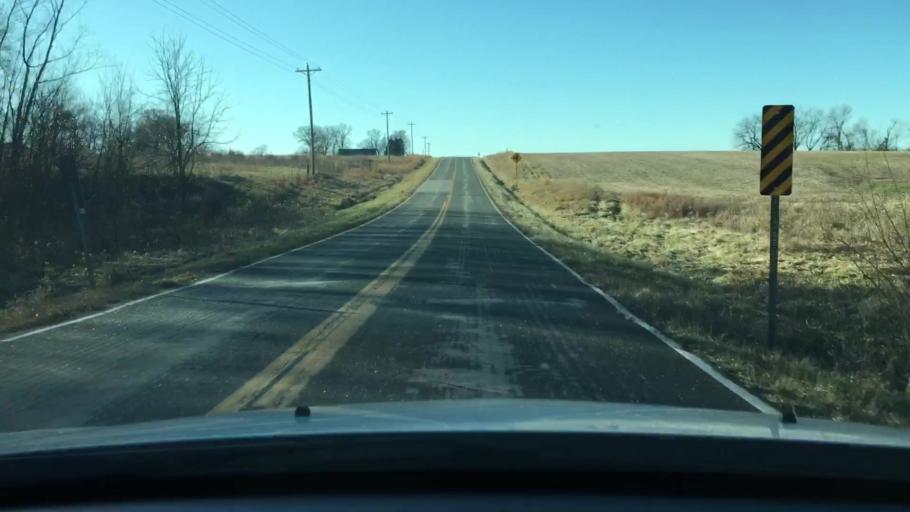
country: US
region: Missouri
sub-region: Audrain County
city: Mexico
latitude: 39.2806
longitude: -91.7633
